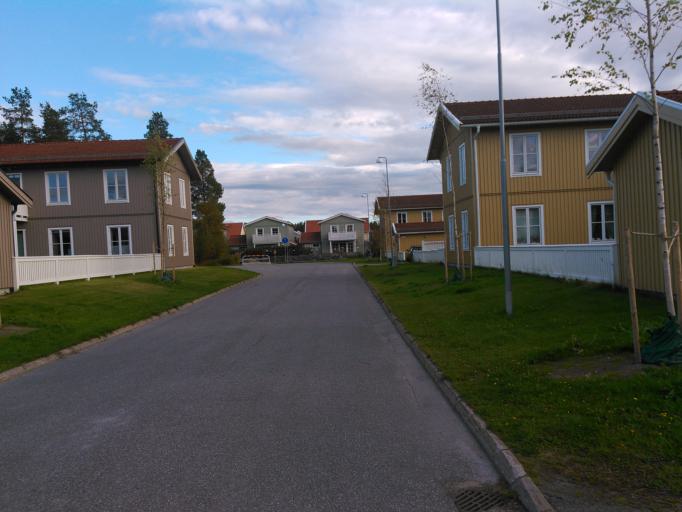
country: SE
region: Vaesterbotten
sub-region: Umea Kommun
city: Ersmark
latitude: 63.8072
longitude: 20.3380
